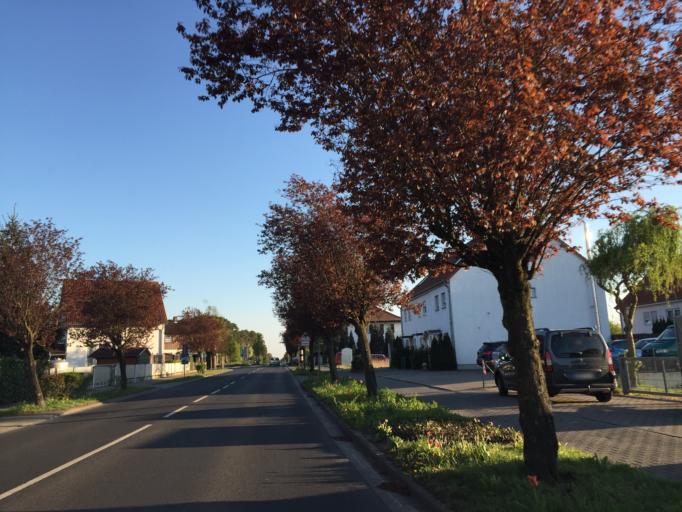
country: DE
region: Hesse
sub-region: Regierungsbezirk Darmstadt
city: Bickenbach
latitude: 49.7513
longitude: 8.6104
